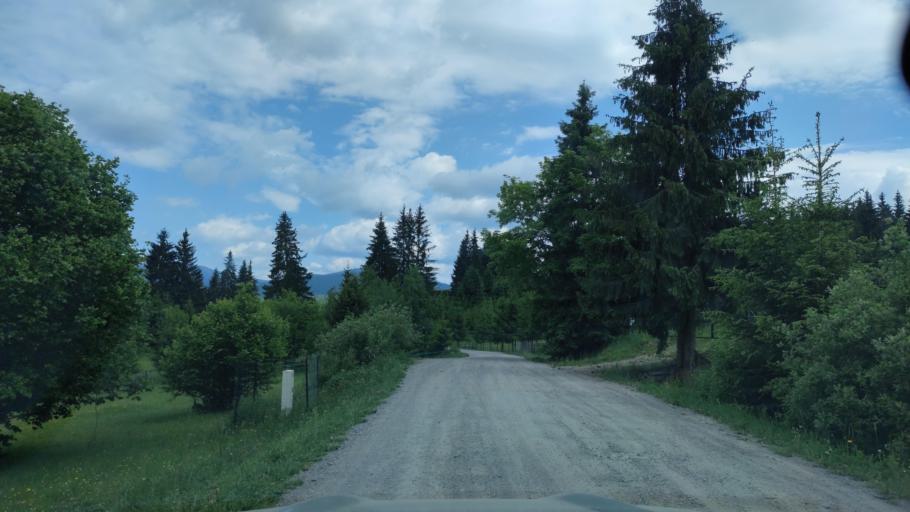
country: RO
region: Harghita
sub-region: Comuna Joseni
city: Joseni
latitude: 46.6655
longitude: 25.3830
